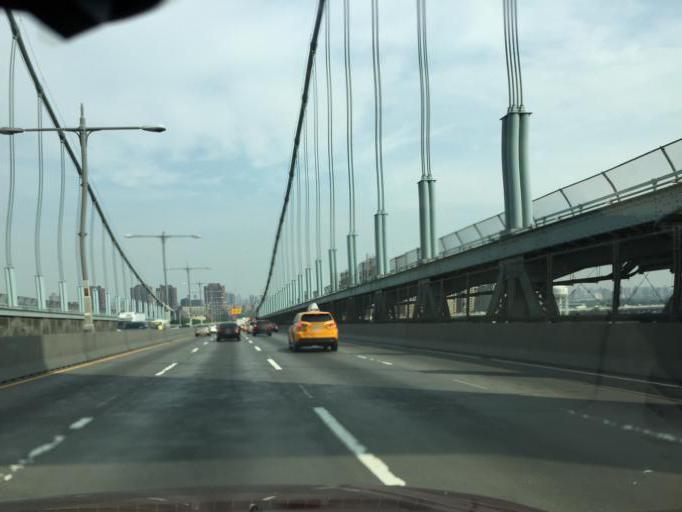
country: US
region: New York
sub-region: New York County
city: Manhattan
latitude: 40.7812
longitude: -73.9278
